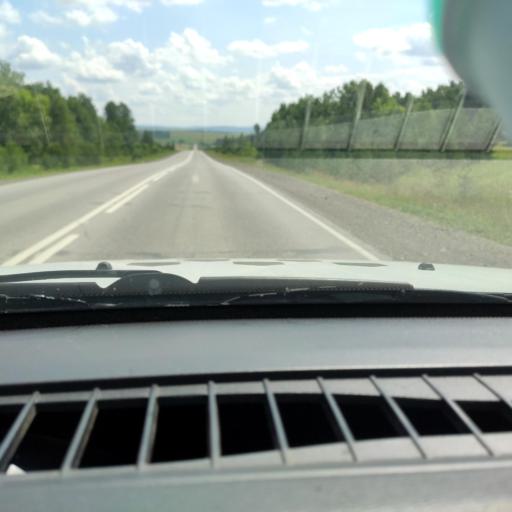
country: RU
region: Bashkortostan
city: Verkhniye Kigi
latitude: 55.3802
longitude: 58.6765
